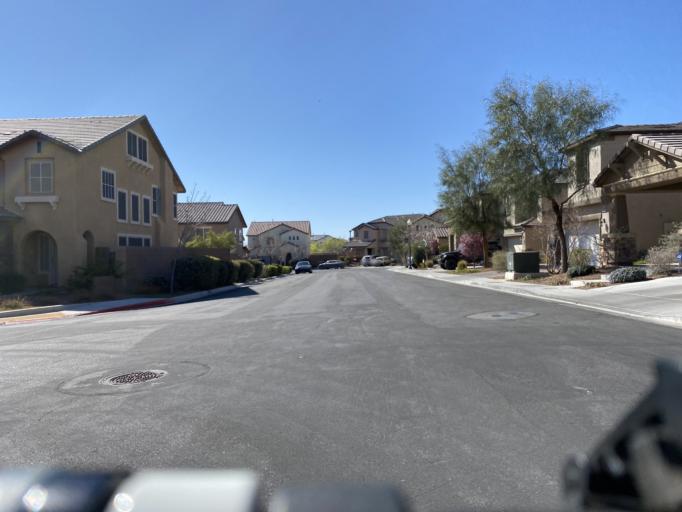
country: US
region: Nevada
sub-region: Clark County
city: Summerlin South
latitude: 36.2895
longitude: -115.3226
